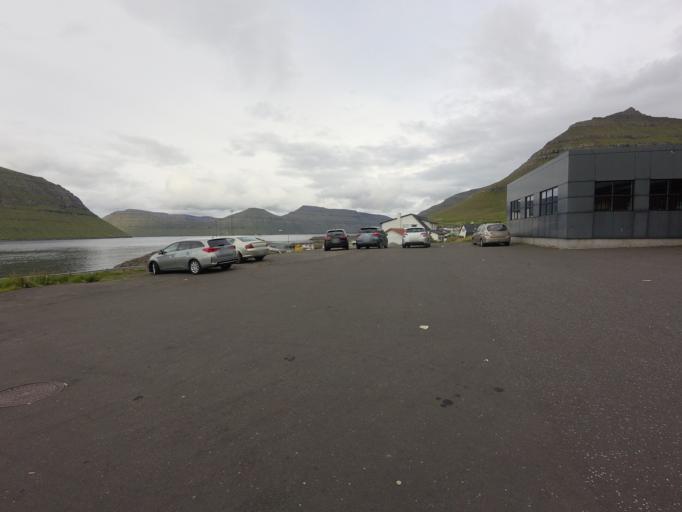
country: FO
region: Eysturoy
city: Eystur
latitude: 62.2131
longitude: -6.7137
